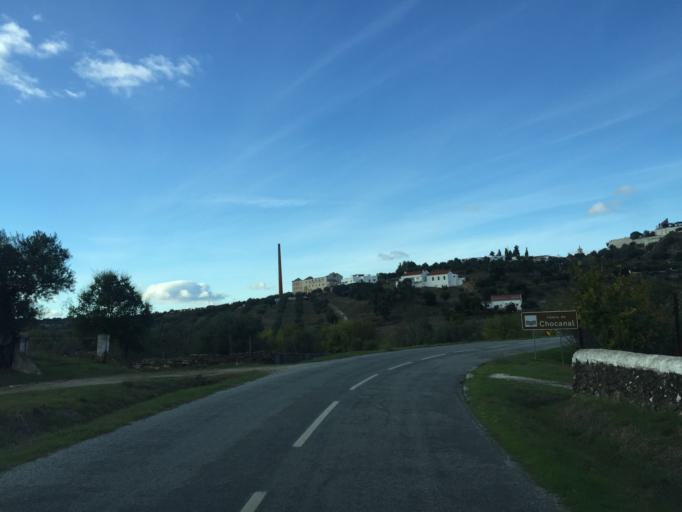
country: PT
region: Portalegre
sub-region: Alter do Chao
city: Alter do Chao
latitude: 39.2790
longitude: -7.6413
